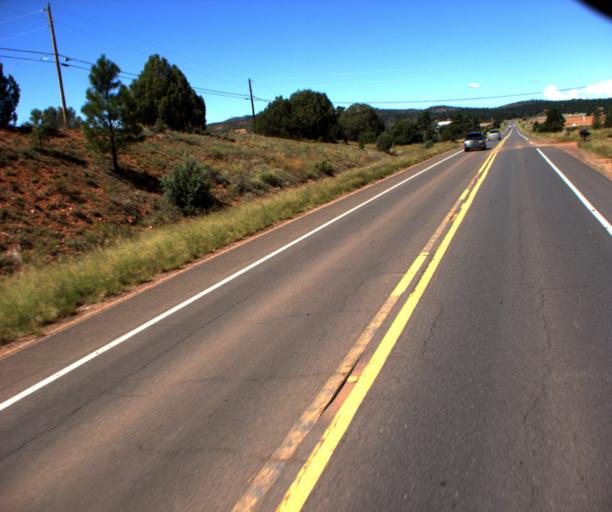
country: US
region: Arizona
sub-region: Navajo County
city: Linden
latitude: 34.2854
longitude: -110.1507
